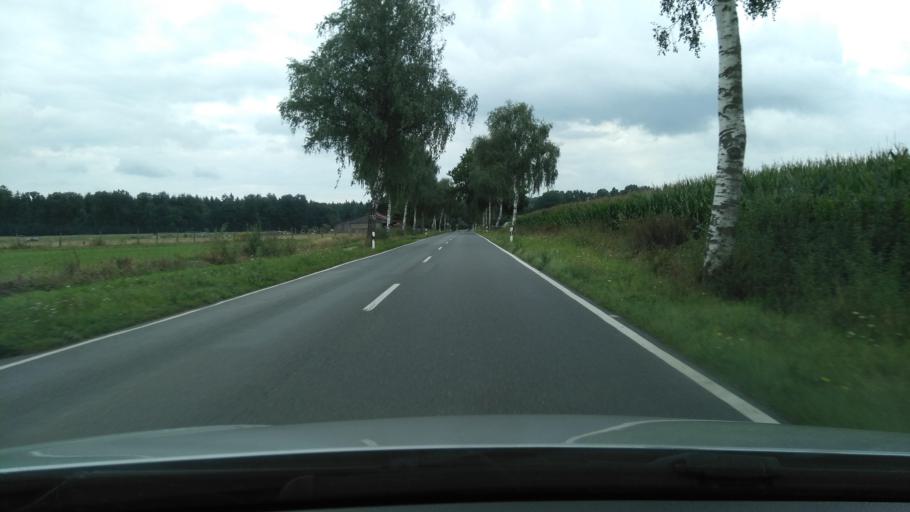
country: DE
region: Lower Saxony
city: Walsrode
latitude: 52.8802
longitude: 9.5777
